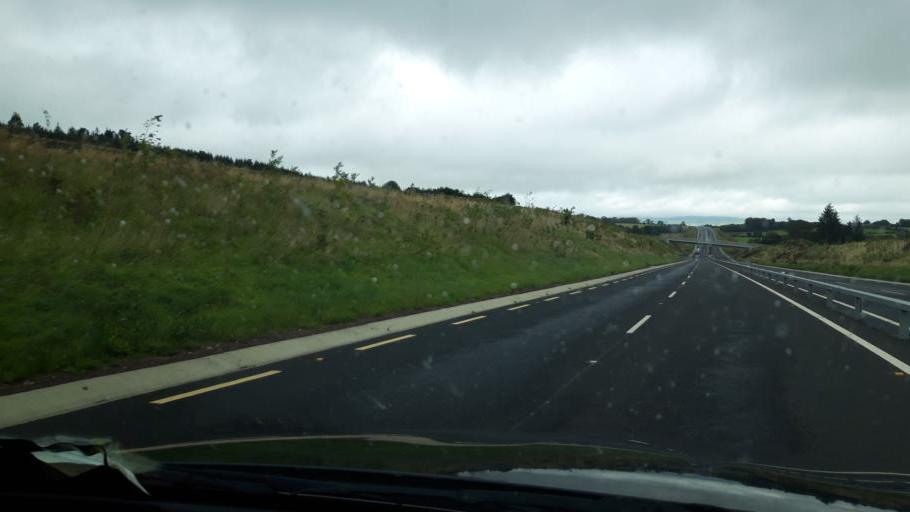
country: IE
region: Leinster
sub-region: Loch Garman
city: New Ross
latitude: 52.3958
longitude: -6.8754
